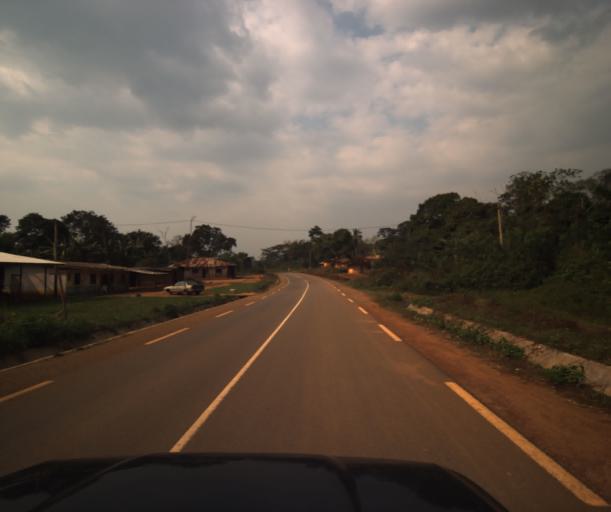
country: CM
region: Centre
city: Mbankomo
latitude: 3.7571
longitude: 11.4057
